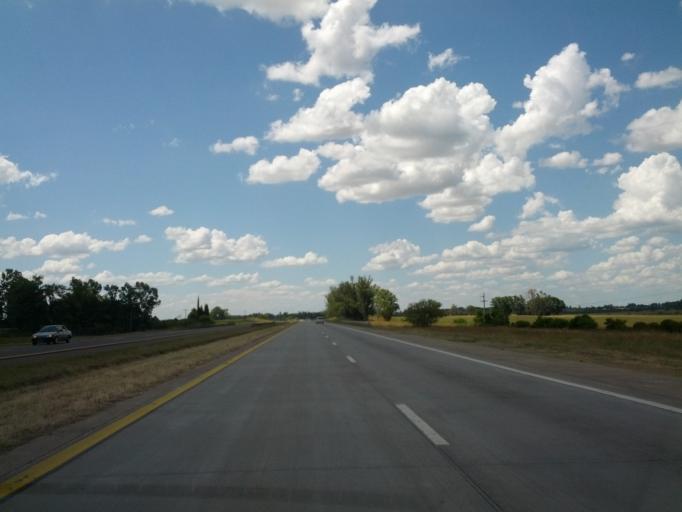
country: UY
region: Paysandu
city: San Felix
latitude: -32.3205
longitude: -58.2570
